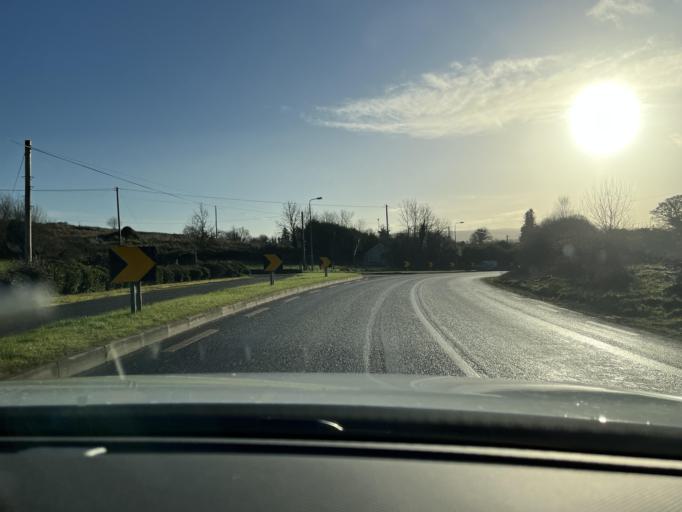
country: IE
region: Connaught
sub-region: County Leitrim
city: Manorhamilton
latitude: 54.2332
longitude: -8.2071
